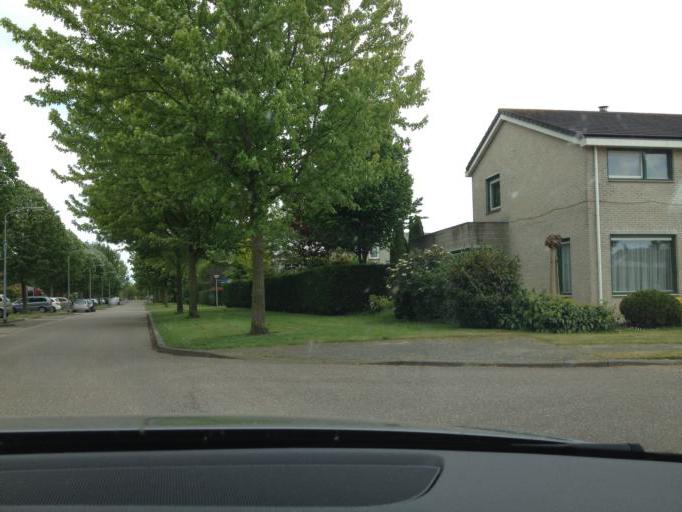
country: NL
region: Flevoland
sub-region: Gemeente Almere
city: Almere Stad
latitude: 52.3648
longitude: 5.2373
